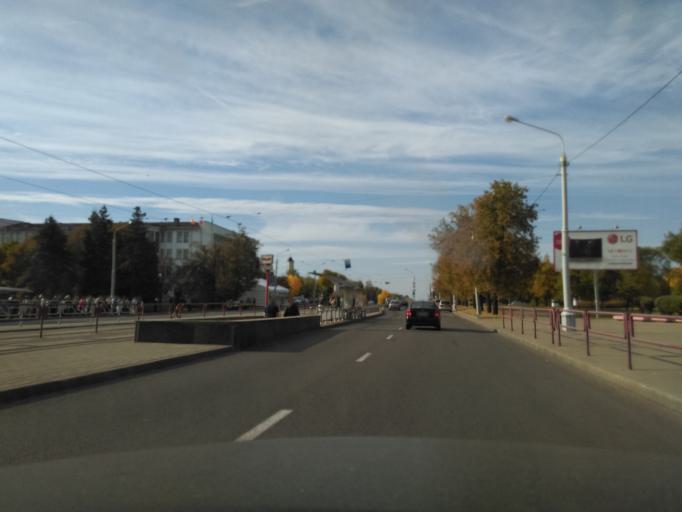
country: BY
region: Minsk
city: Minsk
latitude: 53.8894
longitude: 27.6154
